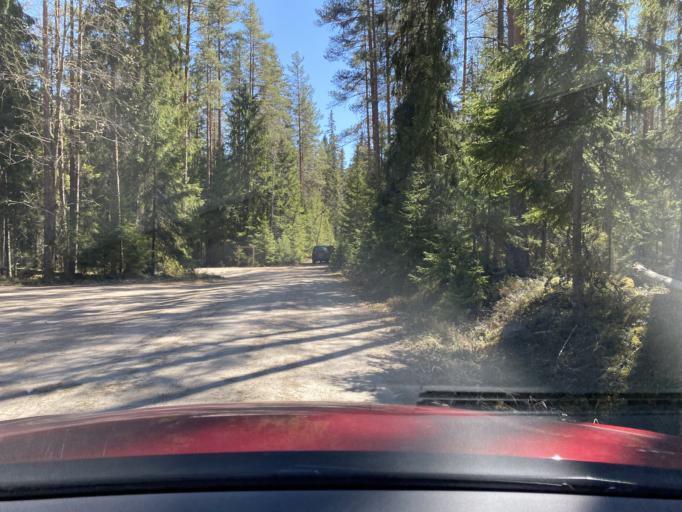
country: FI
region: Uusimaa
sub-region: Helsinki
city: Kaerkoelae
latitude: 60.6530
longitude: 23.8781
